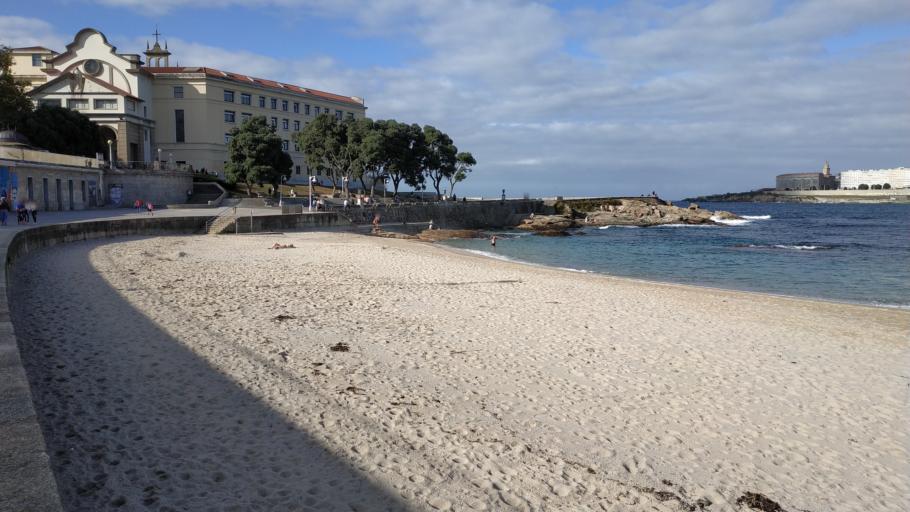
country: ES
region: Galicia
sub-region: Provincia da Coruna
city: A Coruna
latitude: 43.3692
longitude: -8.4144
